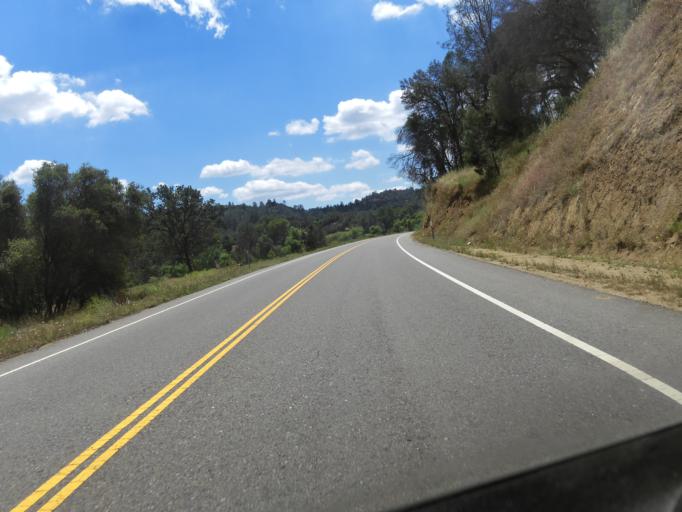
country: US
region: California
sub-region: Madera County
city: Coarsegold
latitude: 37.1631
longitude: -119.6418
